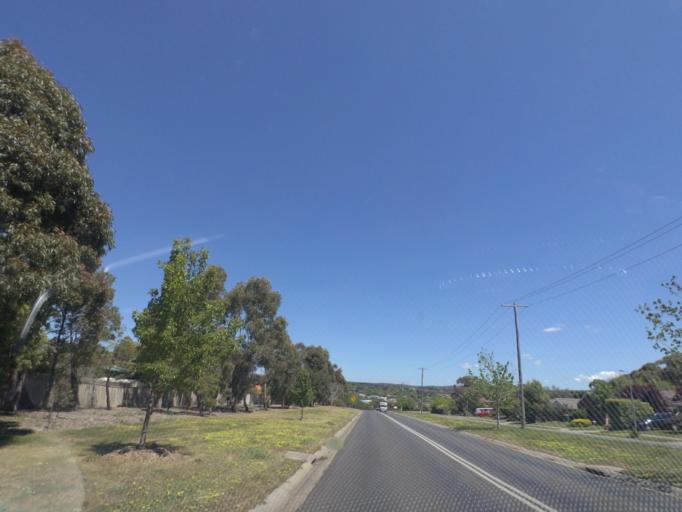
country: AU
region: Victoria
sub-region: Hume
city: Sunbury
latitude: -37.4843
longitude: 144.6003
